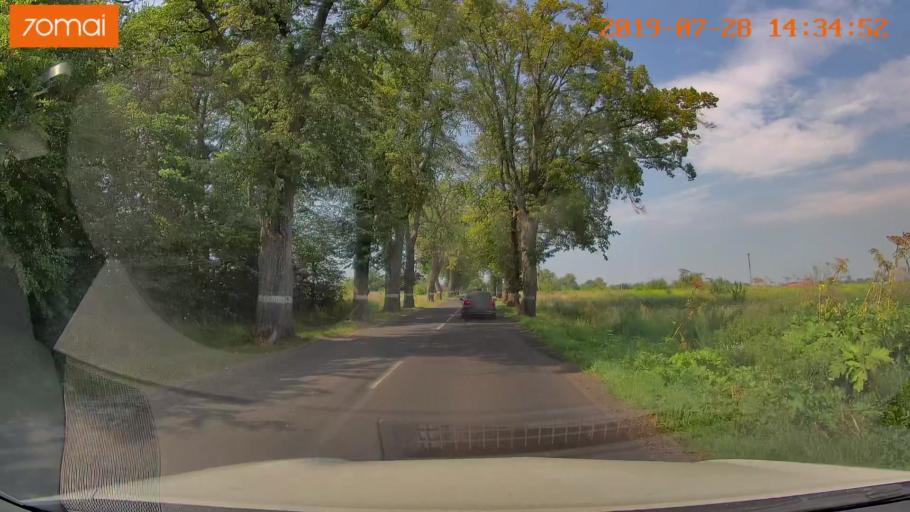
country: RU
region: Kaliningrad
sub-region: Gorod Kaliningrad
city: Yantarnyy
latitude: 54.8277
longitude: 20.0136
